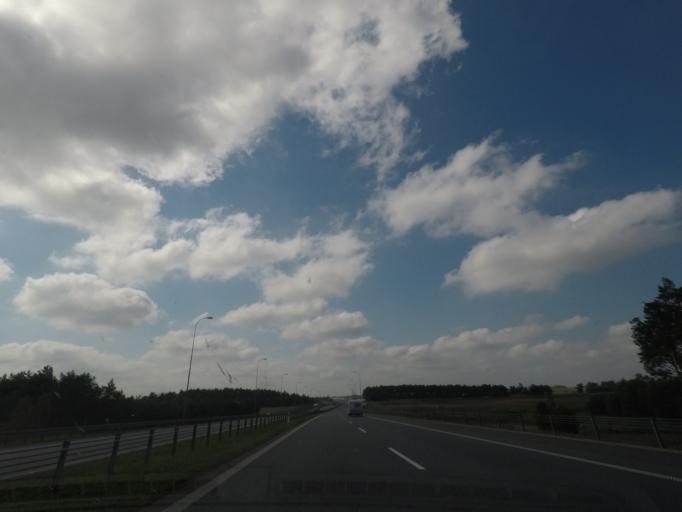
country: PL
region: Kujawsko-Pomorskie
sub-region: Powiat torunski
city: Lubicz Dolny
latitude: 53.1486
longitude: 18.7446
